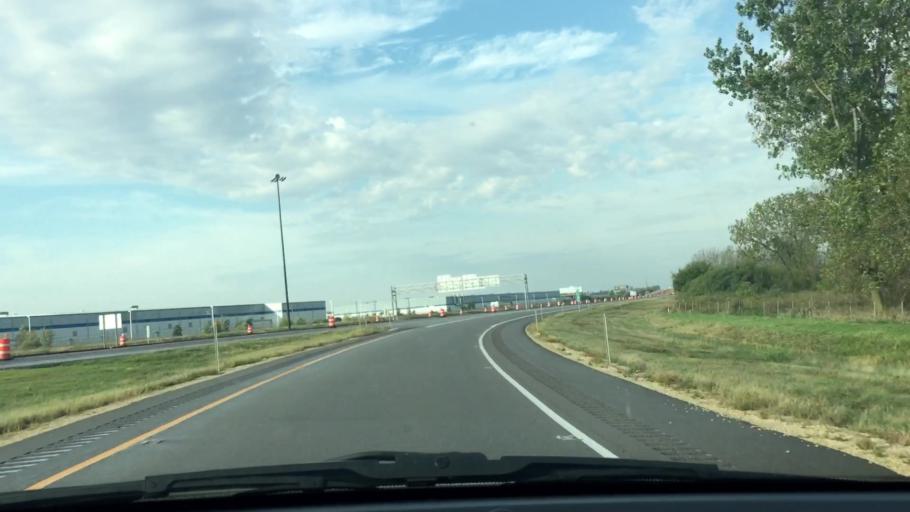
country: US
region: Illinois
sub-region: Ogle County
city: Rochelle
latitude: 41.9048
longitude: -89.0268
